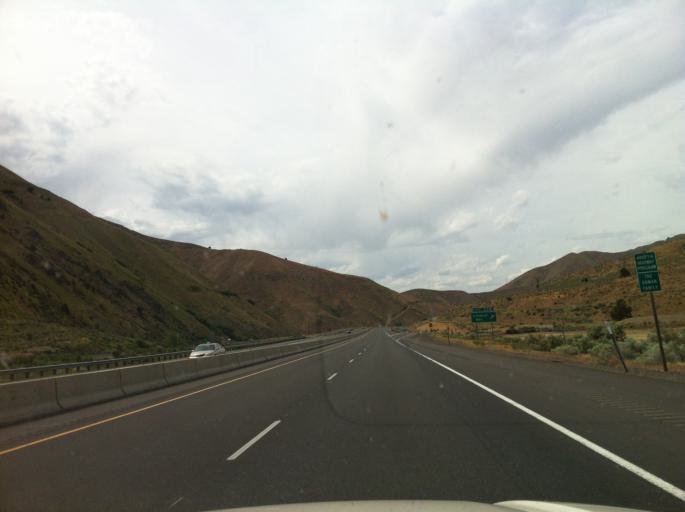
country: US
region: Idaho
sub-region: Washington County
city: Weiser
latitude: 44.4245
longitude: -117.3129
